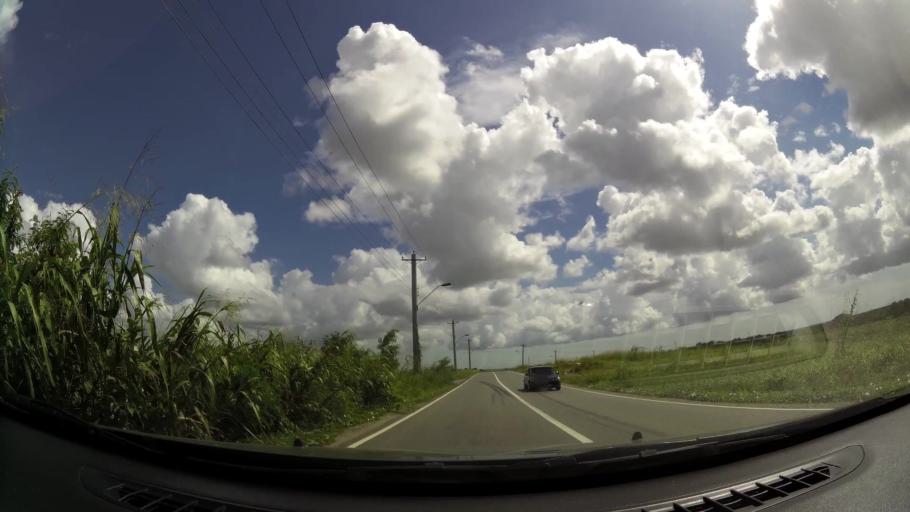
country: TT
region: City of San Fernando
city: San Fernando
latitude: 10.2402
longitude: -61.4981
